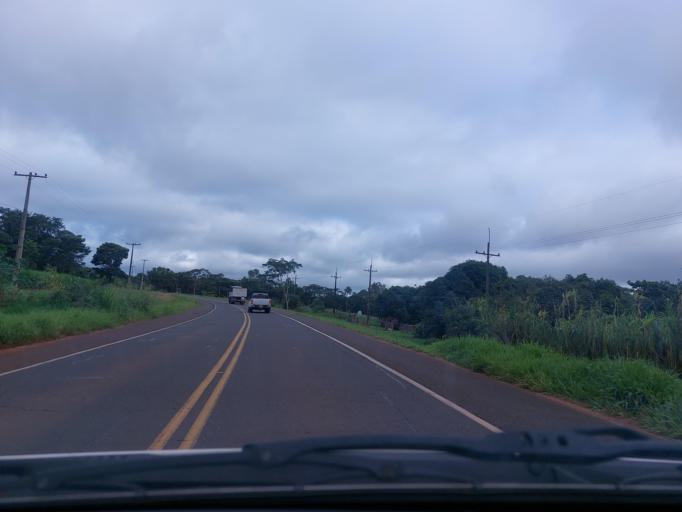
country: PY
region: San Pedro
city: Guayaybi
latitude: -24.6516
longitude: -56.3876
